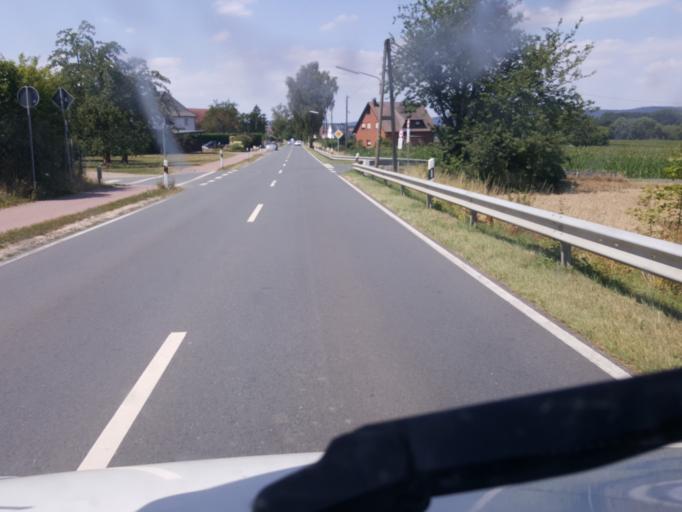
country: DE
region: North Rhine-Westphalia
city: Bad Oeynhausen
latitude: 52.2305
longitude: 8.7604
